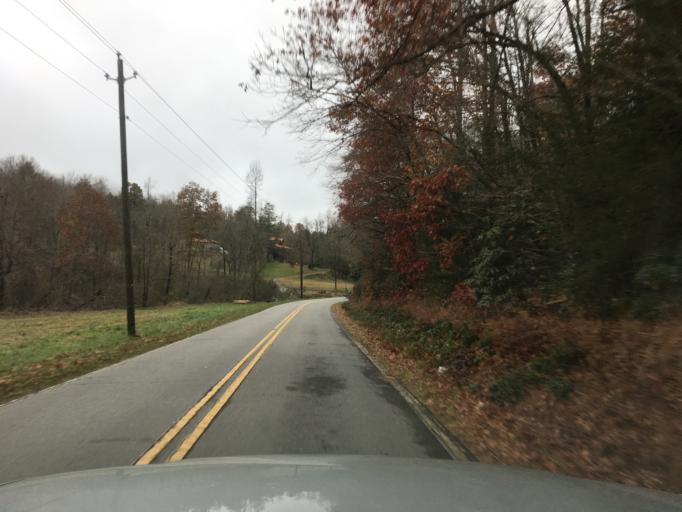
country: US
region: North Carolina
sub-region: Rutherford County
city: Lake Lure
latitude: 35.5283
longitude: -82.2426
